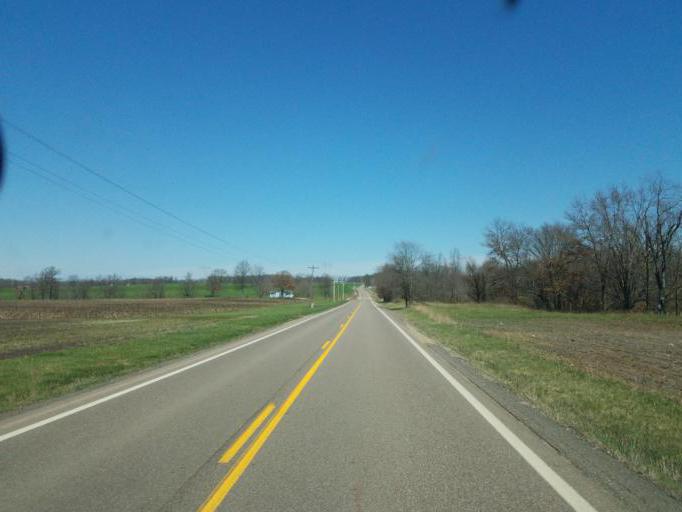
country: US
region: Ohio
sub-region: Knox County
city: Oak Hill
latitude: 40.3398
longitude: -82.3014
